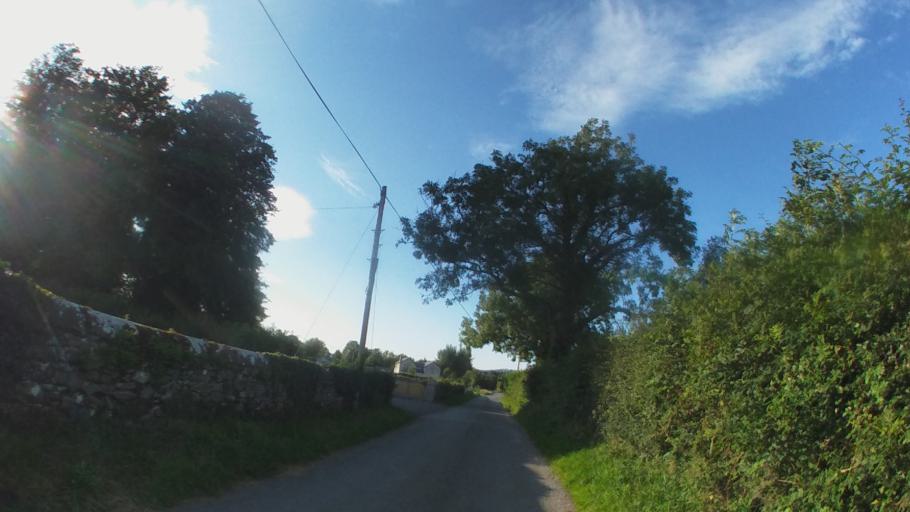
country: IE
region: Leinster
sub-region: Kilkenny
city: Kilkenny
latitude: 52.6872
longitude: -7.1874
